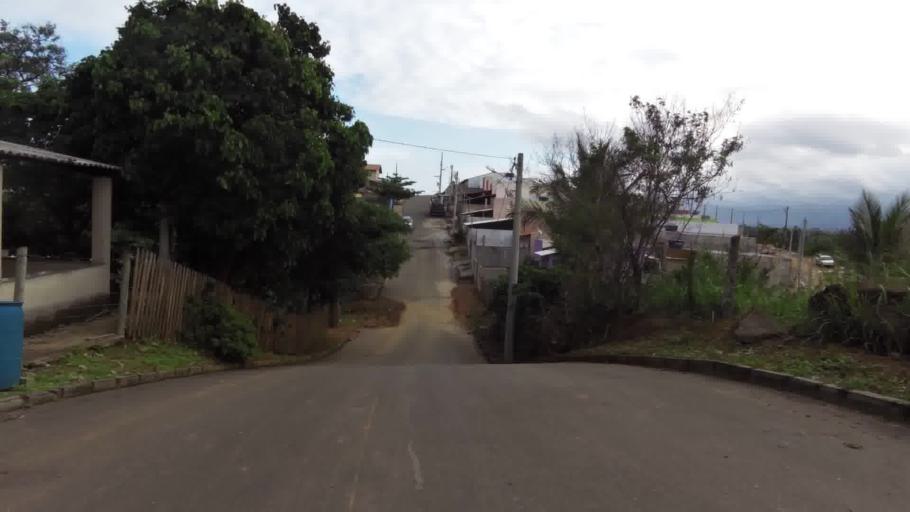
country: BR
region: Espirito Santo
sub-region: Piuma
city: Piuma
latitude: -20.7954
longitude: -40.6426
